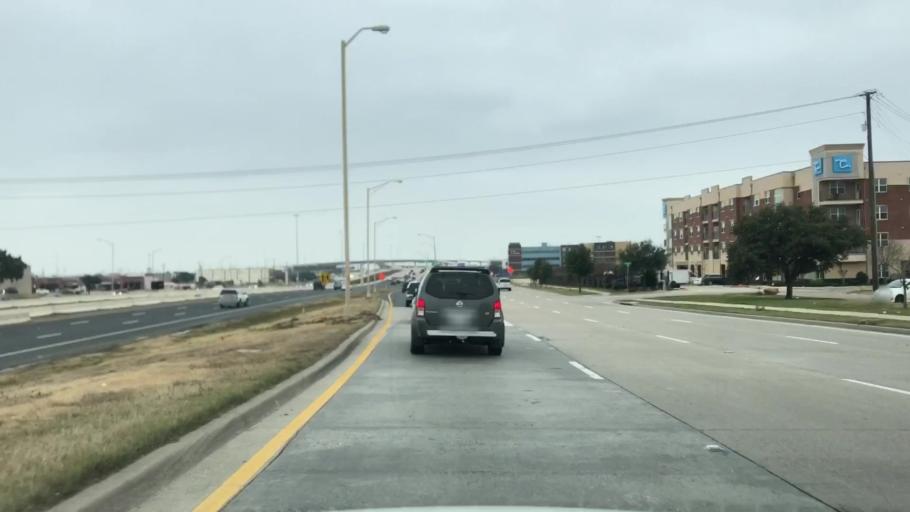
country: US
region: Texas
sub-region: Dallas County
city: Carrollton
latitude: 32.9836
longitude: -96.9121
